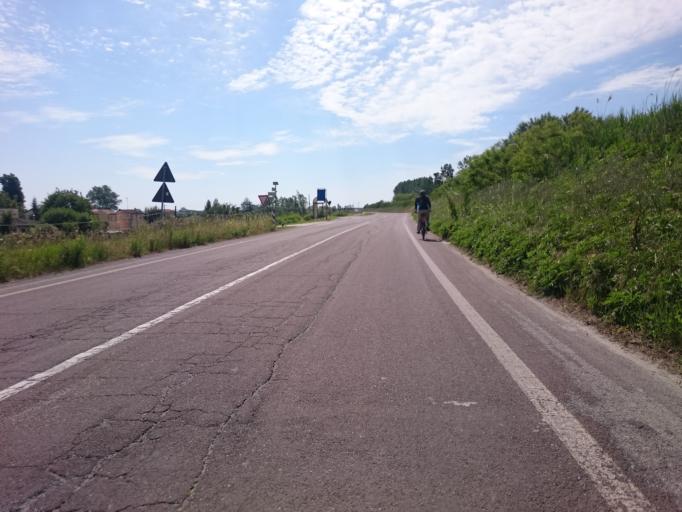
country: IT
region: Veneto
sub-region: Provincia di Rovigo
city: Ariano
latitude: 44.9598
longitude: 12.1153
